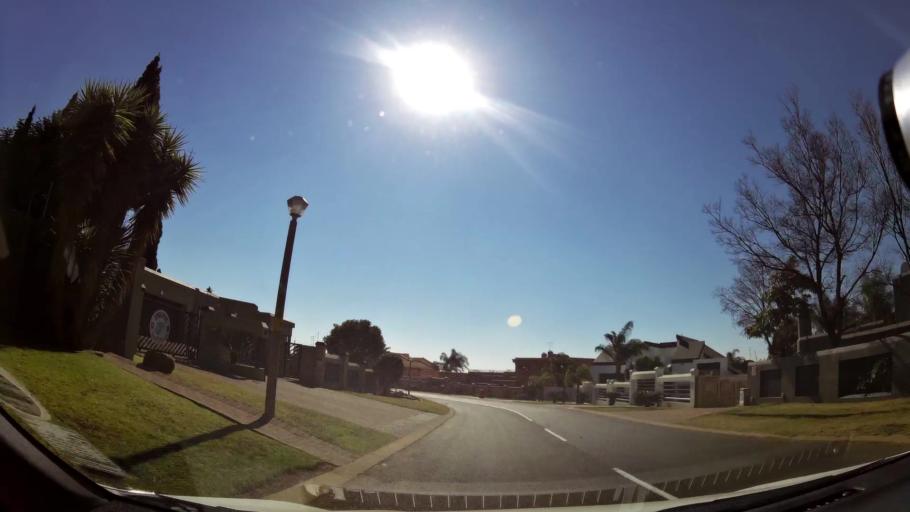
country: ZA
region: Gauteng
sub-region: Ekurhuleni Metropolitan Municipality
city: Germiston
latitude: -26.2927
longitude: 28.1003
